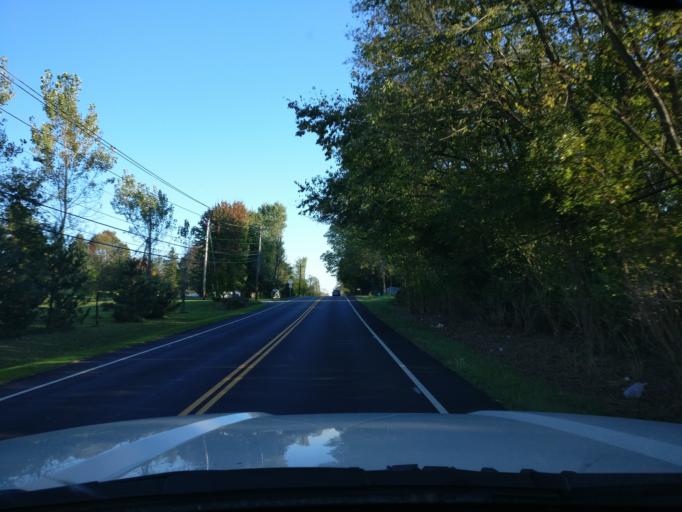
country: US
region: Ohio
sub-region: Warren County
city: Hunter
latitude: 39.5260
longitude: -84.2794
